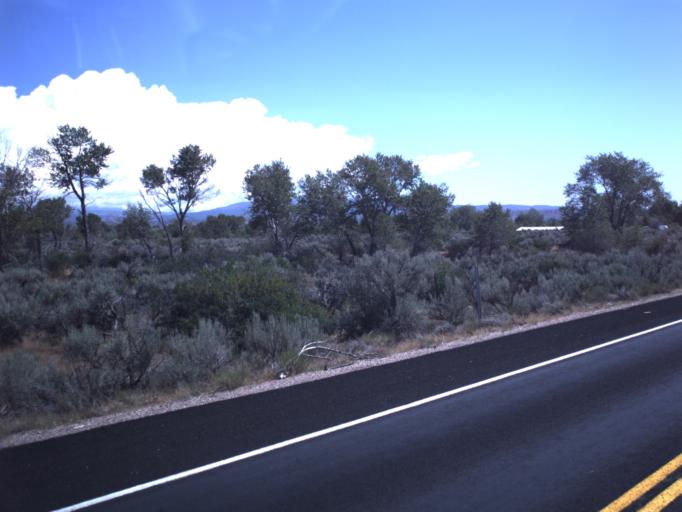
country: US
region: Utah
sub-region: Duchesne County
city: Roosevelt
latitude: 40.4038
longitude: -109.8954
